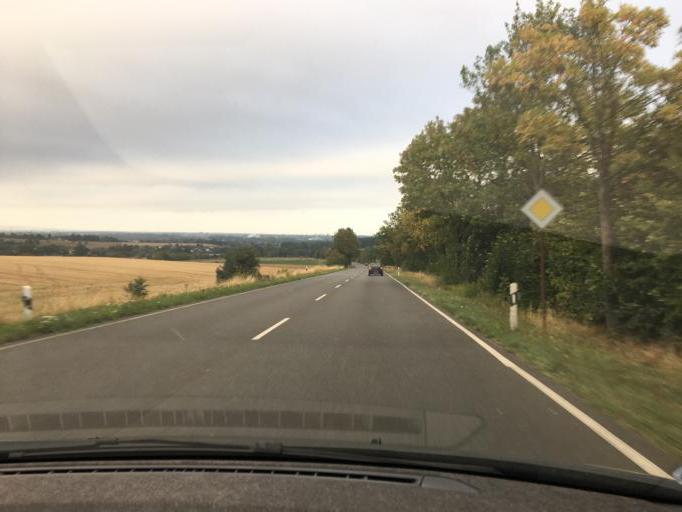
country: DE
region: North Rhine-Westphalia
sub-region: Regierungsbezirk Koln
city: Kreuzau
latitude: 50.7410
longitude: 6.4601
